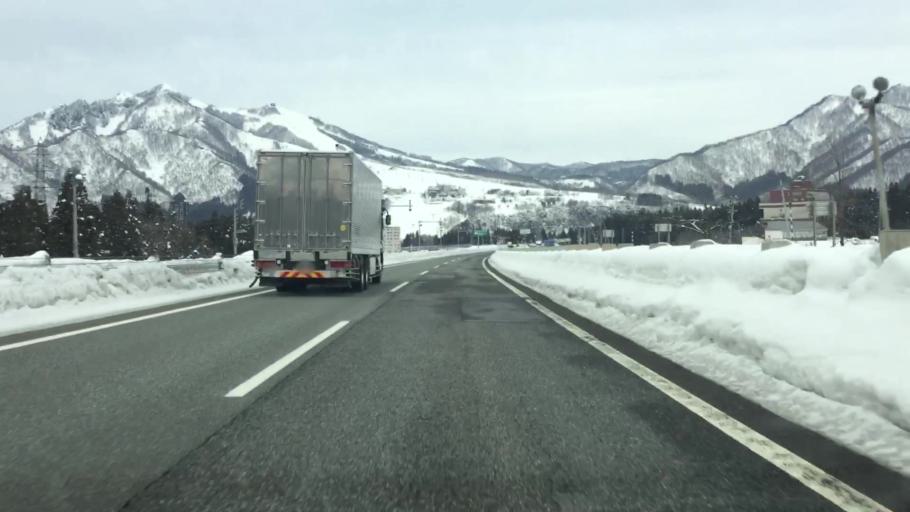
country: JP
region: Niigata
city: Shiozawa
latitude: 36.9171
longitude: 138.8399
